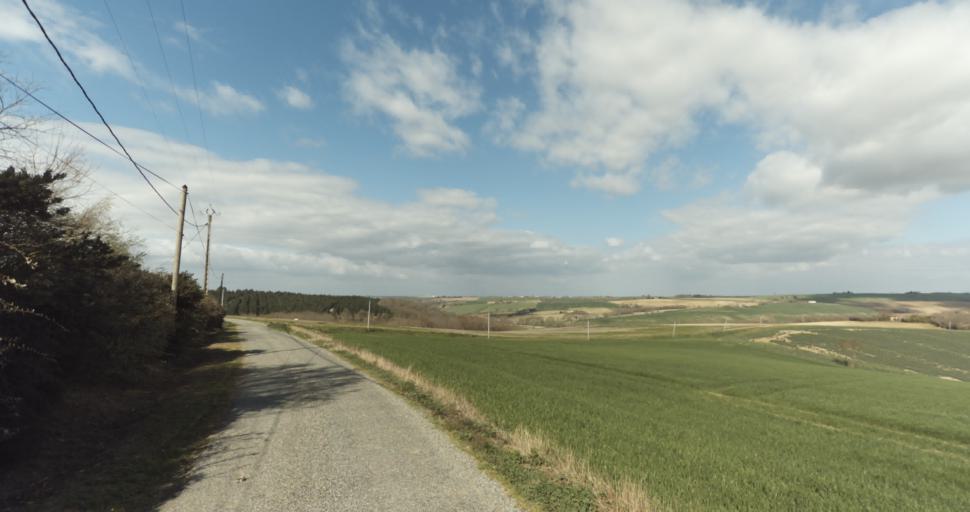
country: FR
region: Midi-Pyrenees
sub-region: Departement de la Haute-Garonne
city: Auterive
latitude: 43.3657
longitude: 1.5096
